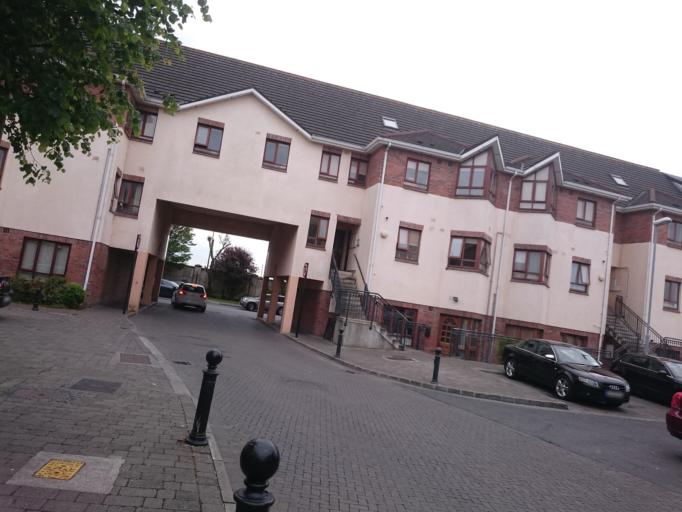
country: IE
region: Leinster
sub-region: Kilkenny
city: Kilkenny
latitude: 52.6494
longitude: -7.2544
